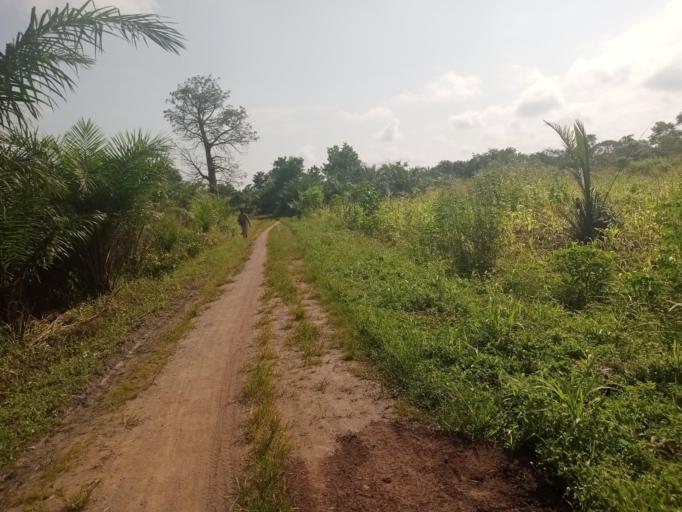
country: TG
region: Maritime
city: Tsevie
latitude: 6.6619
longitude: 0.9724
